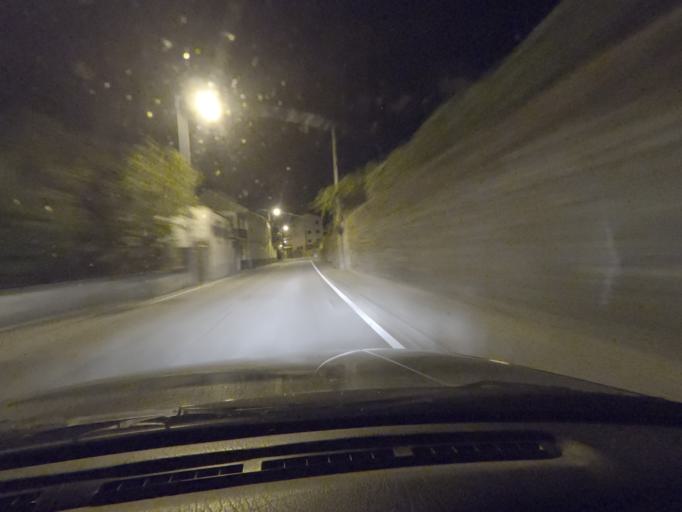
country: PT
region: Vila Real
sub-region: Peso da Regua
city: Godim
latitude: 41.1813
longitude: -7.7942
